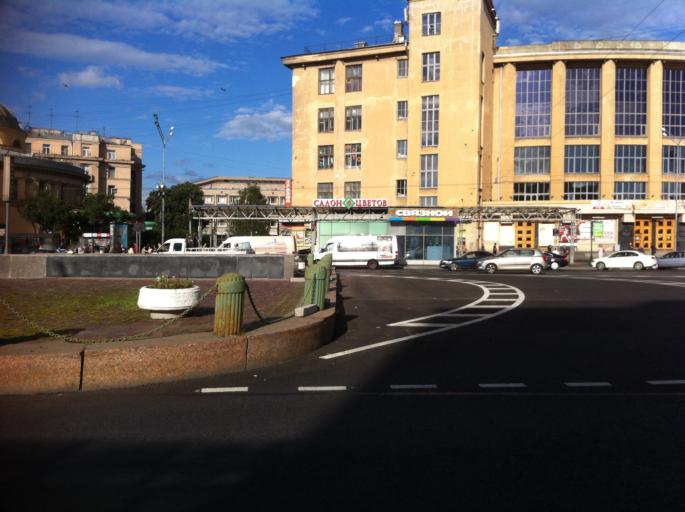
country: RU
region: St.-Petersburg
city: Admiralteisky
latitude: 59.9004
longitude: 30.2740
